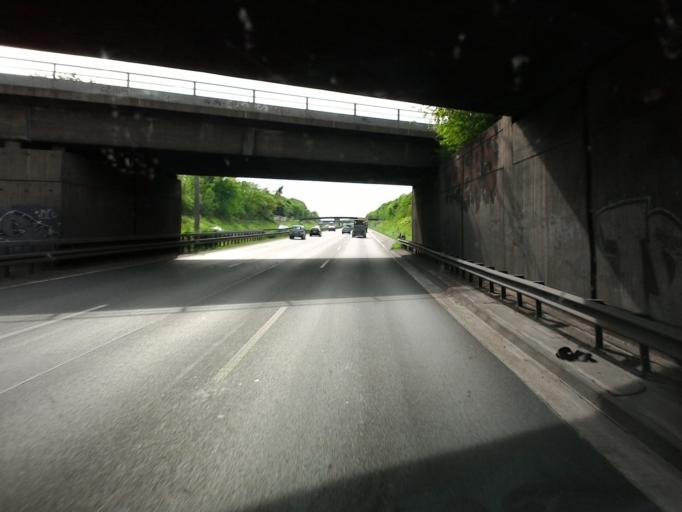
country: DE
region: North Rhine-Westphalia
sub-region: Regierungsbezirk Dusseldorf
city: Moers
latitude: 51.4369
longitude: 6.6559
